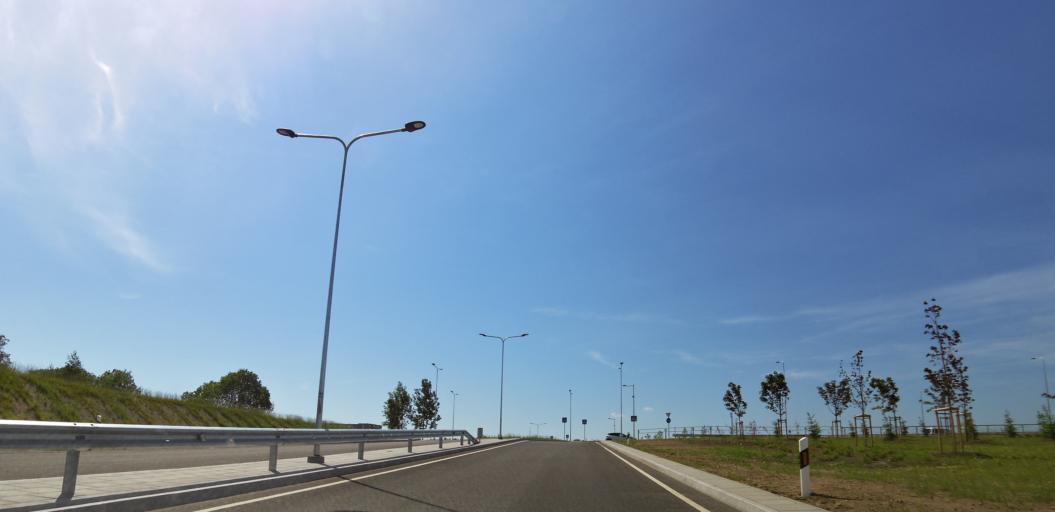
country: LT
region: Vilnius County
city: Justiniskes
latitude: 54.7255
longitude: 25.2087
